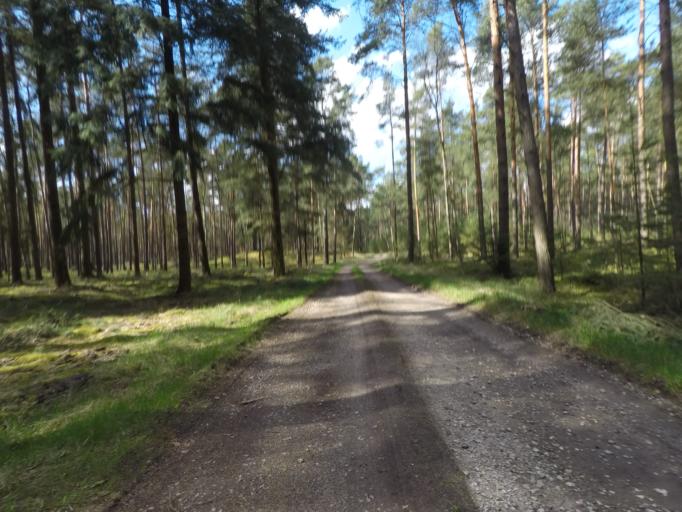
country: DE
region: Brandenburg
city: Melchow
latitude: 52.8237
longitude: 13.6711
